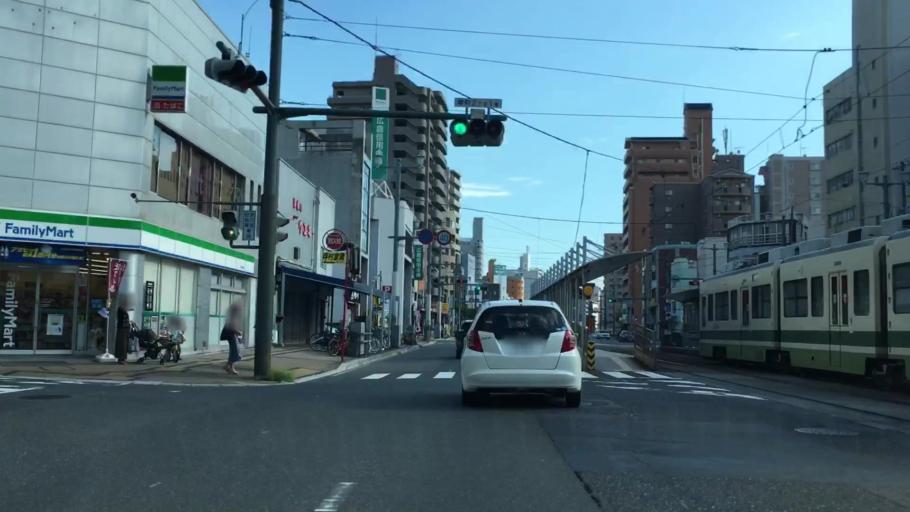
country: JP
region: Hiroshima
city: Hiroshima-shi
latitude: 34.3948
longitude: 132.4464
